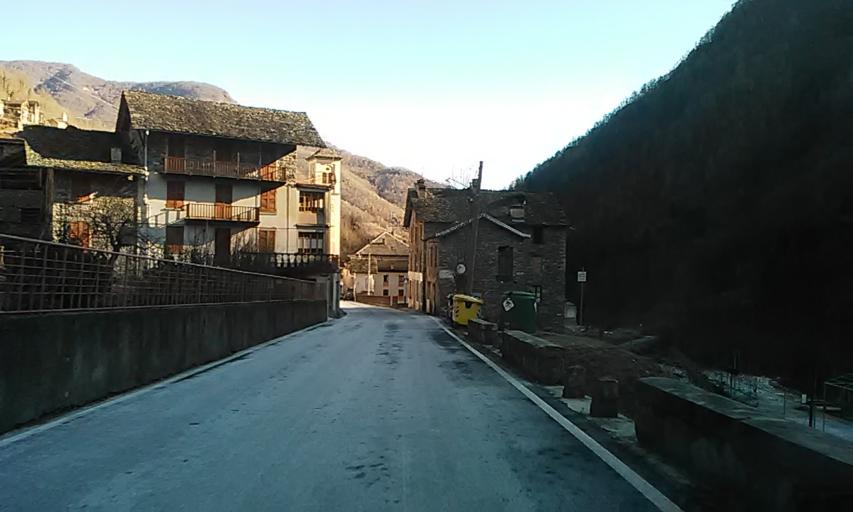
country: IT
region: Piedmont
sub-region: Provincia di Vercelli
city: Boccioleto
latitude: 45.8302
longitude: 8.1113
